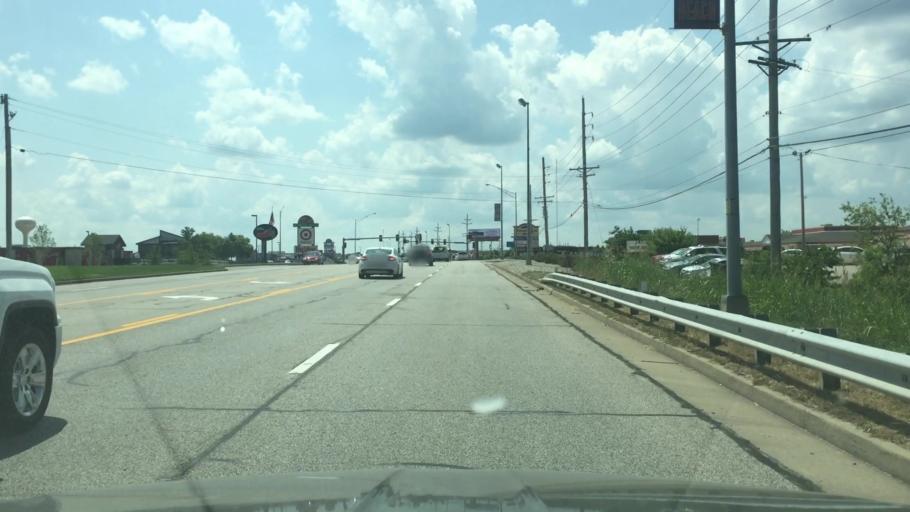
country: US
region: Missouri
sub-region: Miller County
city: Lake Ozark
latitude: 38.1633
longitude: -92.6088
